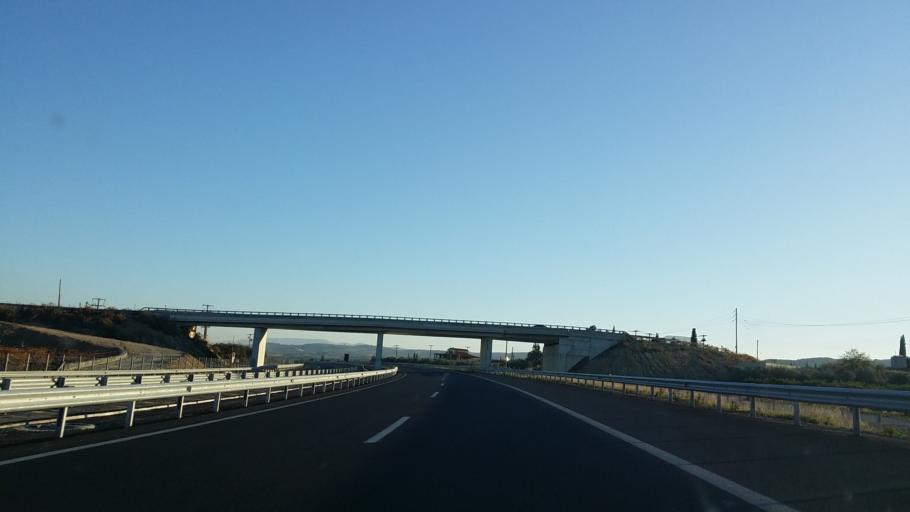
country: GR
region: Peloponnese
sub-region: Nomos Korinthias
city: Velo
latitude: 37.9613
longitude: 22.7486
